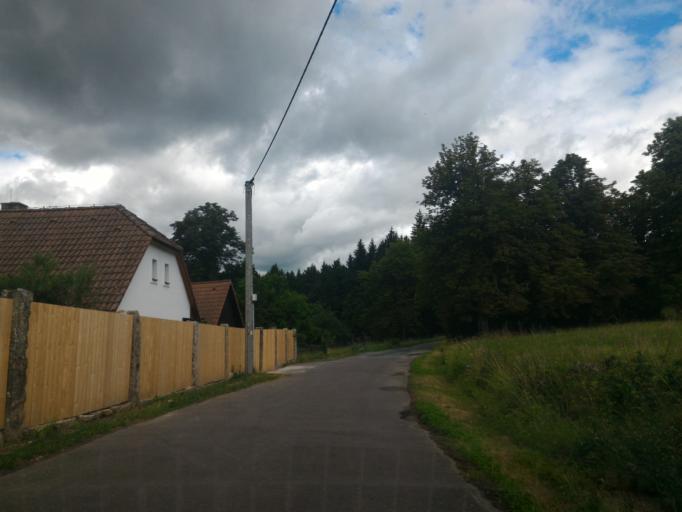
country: CZ
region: Vysocina
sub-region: Okres Jihlava
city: Telc
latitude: 49.2450
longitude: 15.4263
